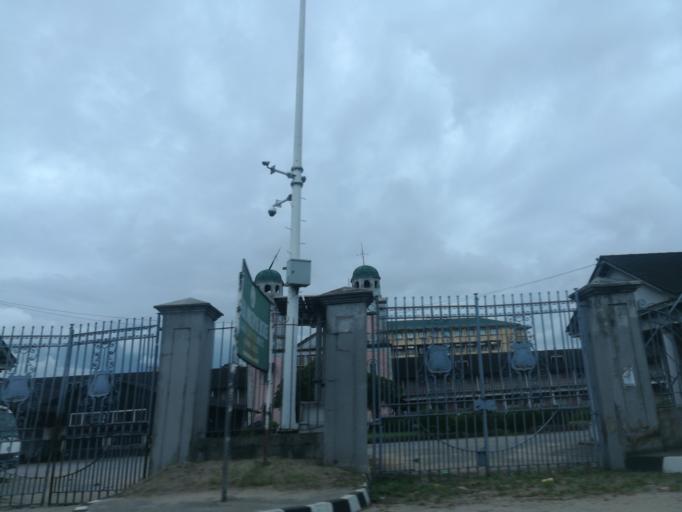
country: NG
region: Lagos
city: Lagos
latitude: 6.4479
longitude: 3.3950
